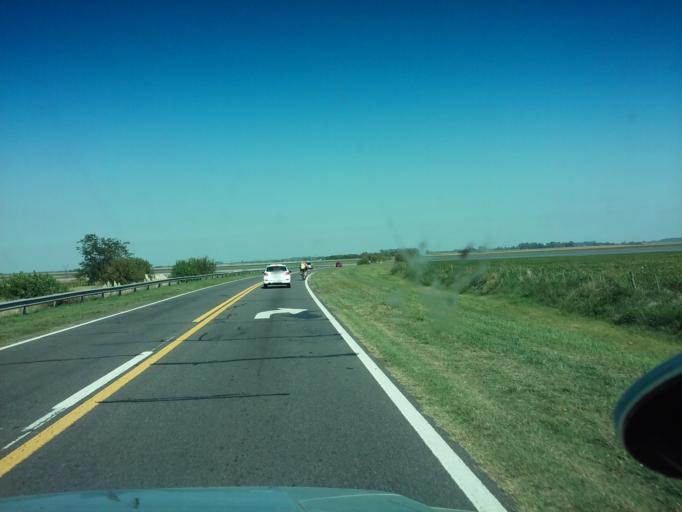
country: AR
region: Buenos Aires
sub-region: Partido de Alberti
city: Alberti
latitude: -35.0610
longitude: -60.2837
